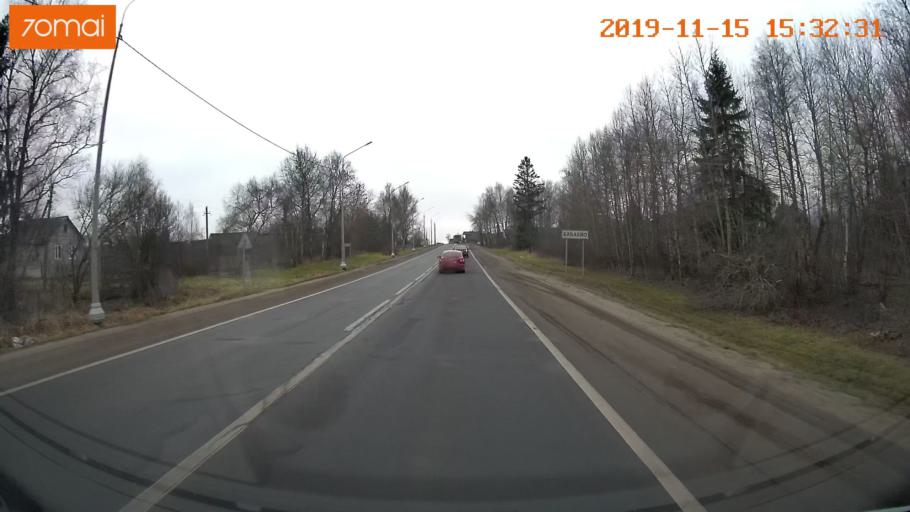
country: RU
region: Jaroslavl
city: Danilov
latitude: 58.0894
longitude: 40.0992
